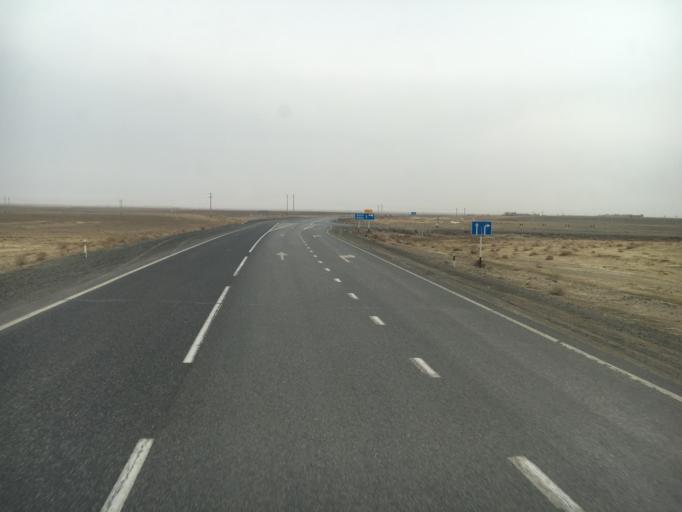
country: KZ
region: Qyzylorda
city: Aral
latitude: 46.8238
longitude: 61.7056
